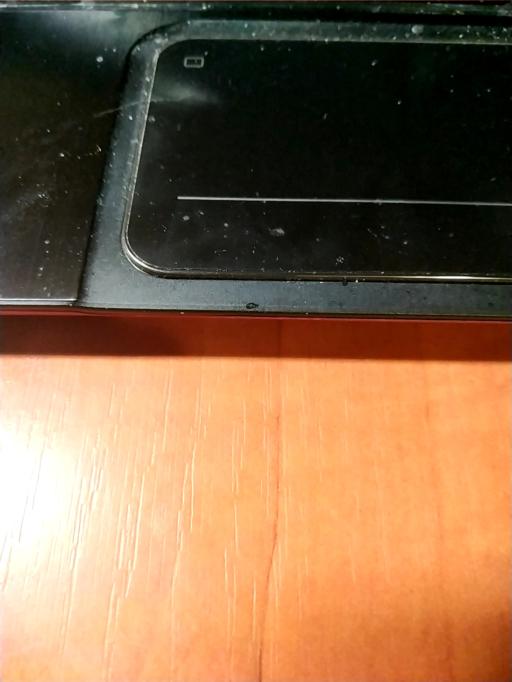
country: RU
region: Tverskaya
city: Ves'yegonsk
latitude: 58.7308
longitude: 37.5438
